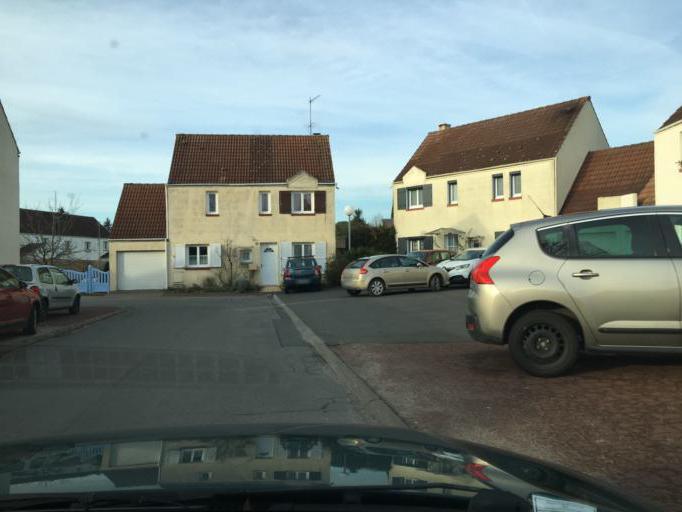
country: FR
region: Centre
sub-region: Departement du Loiret
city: La Ferte-Saint-Aubin
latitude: 47.7177
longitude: 1.9398
